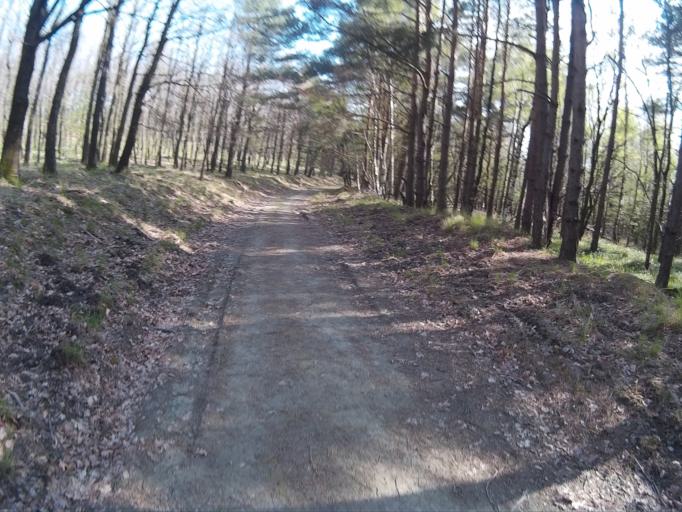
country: AT
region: Burgenland
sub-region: Politischer Bezirk Oberwart
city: Rechnitz
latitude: 47.3341
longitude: 16.4648
